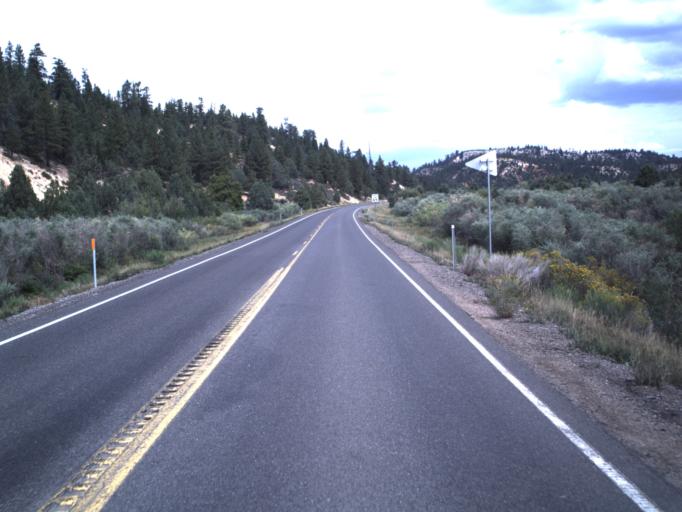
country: US
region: Utah
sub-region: Kane County
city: Kanab
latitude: 37.4302
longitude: -112.5384
